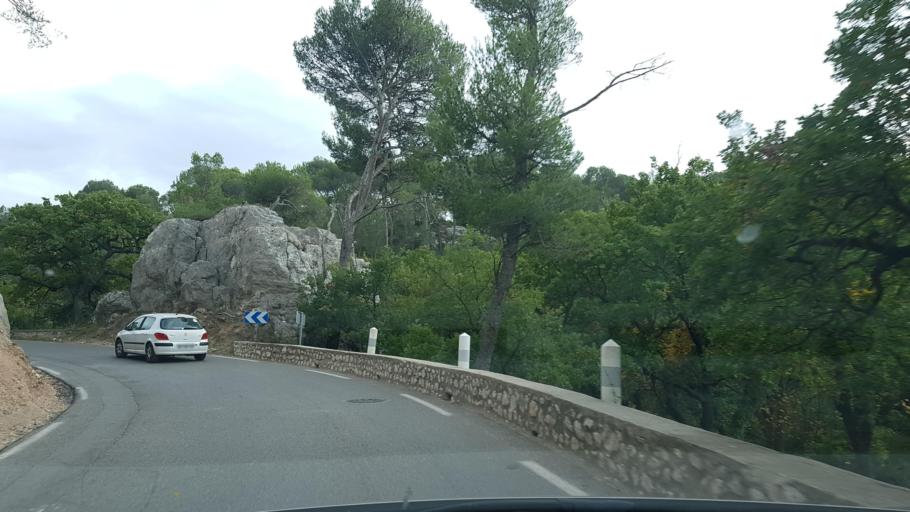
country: FR
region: Provence-Alpes-Cote d'Azur
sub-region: Departement des Bouches-du-Rhone
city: Cabries
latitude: 43.4335
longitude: 5.3793
